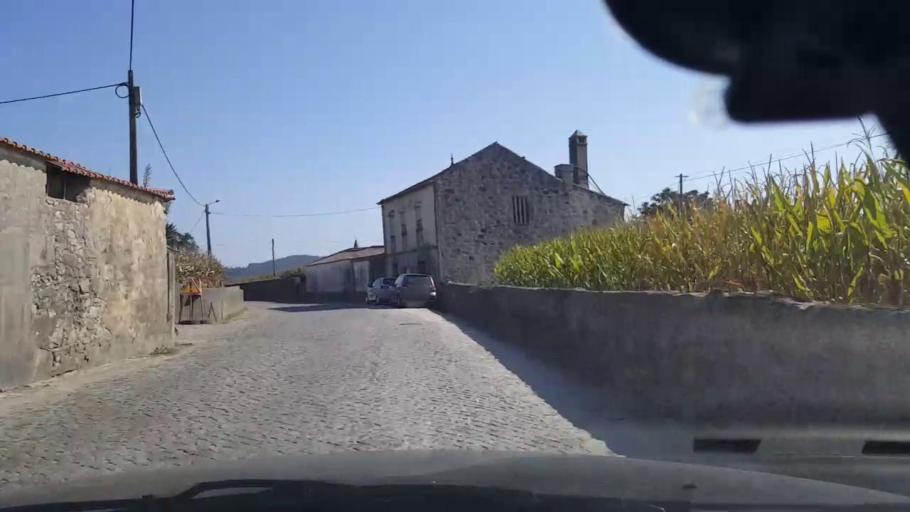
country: PT
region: Porto
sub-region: Povoa de Varzim
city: Pedroso
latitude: 41.4051
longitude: -8.6905
